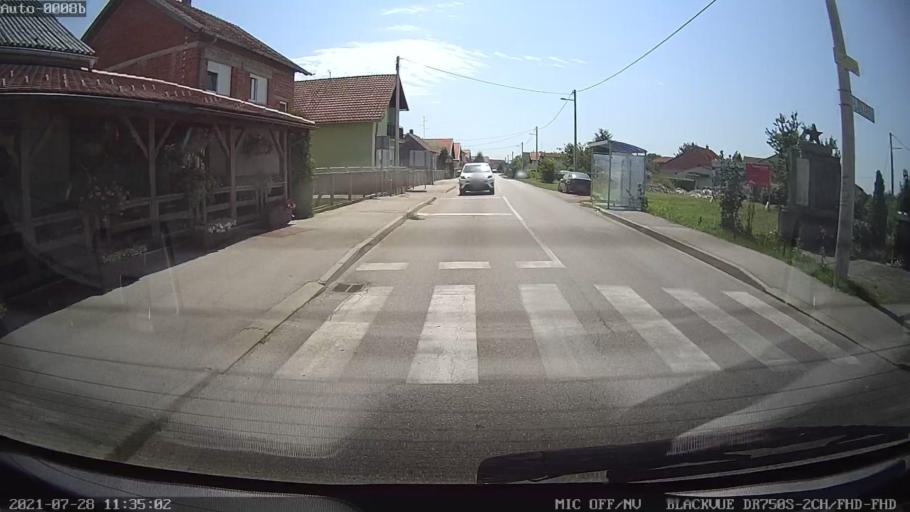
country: HR
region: Varazdinska
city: Varazdin
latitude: 46.2940
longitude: 16.3724
